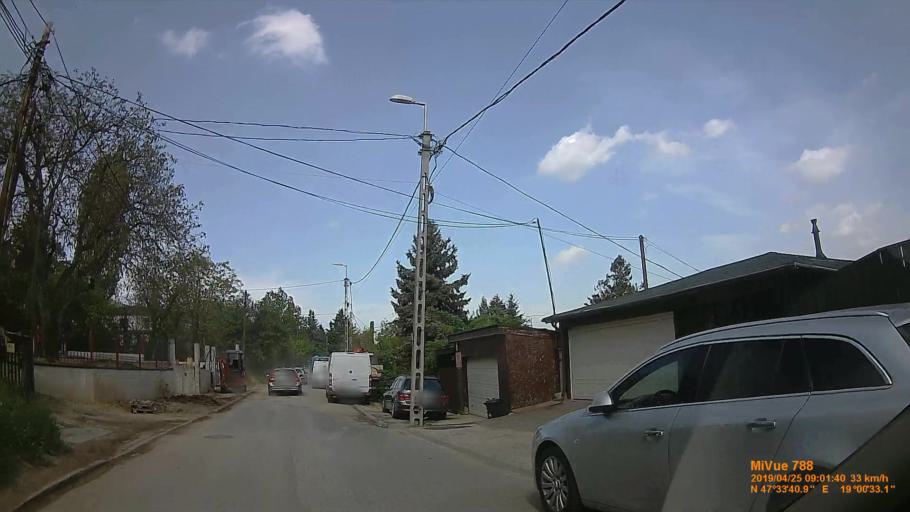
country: HU
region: Pest
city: Urom
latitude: 47.5614
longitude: 19.0091
